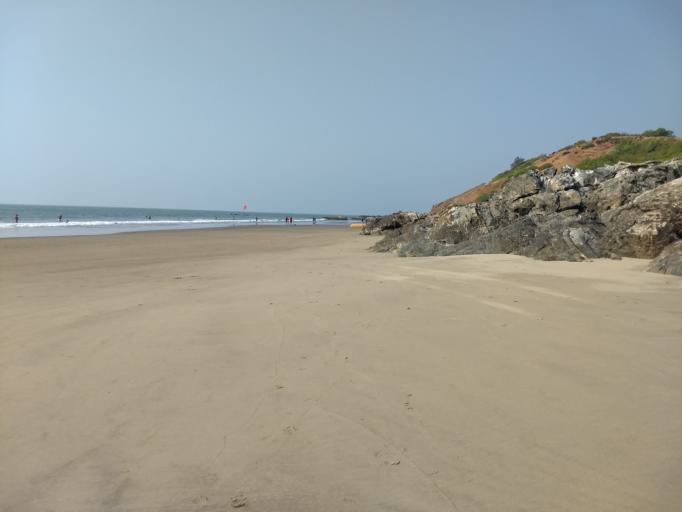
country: IN
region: Goa
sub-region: North Goa
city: Vagator
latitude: 15.6047
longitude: 73.7329
